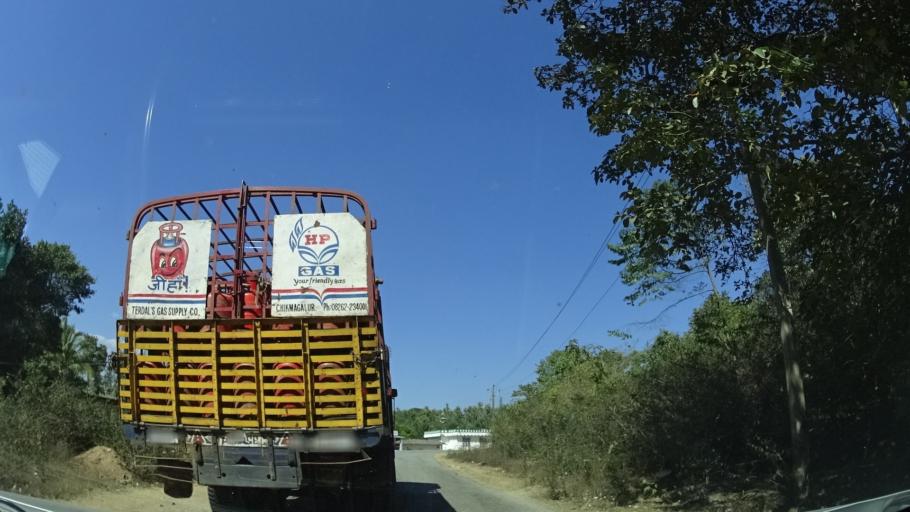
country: IN
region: Karnataka
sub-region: Chikmagalur
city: Mudigere
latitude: 13.1870
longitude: 75.6625
